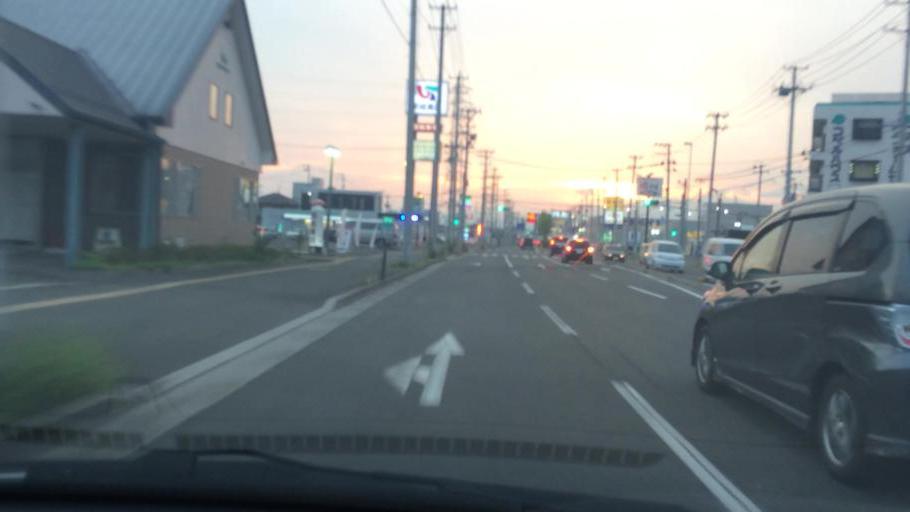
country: JP
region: Miyagi
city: Sendai-shi
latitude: 38.3126
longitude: 140.9116
